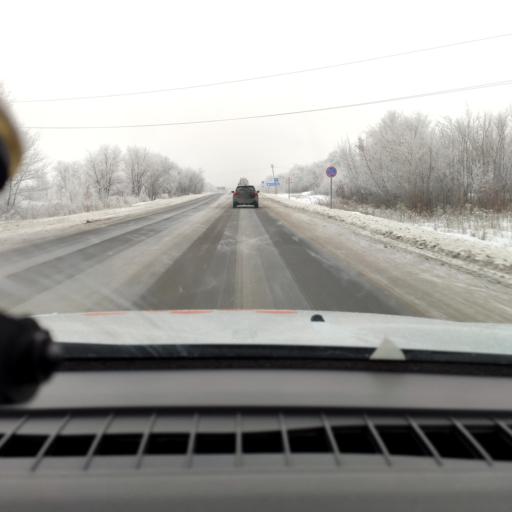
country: RU
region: Samara
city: Samara
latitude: 53.0797
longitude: 50.1647
